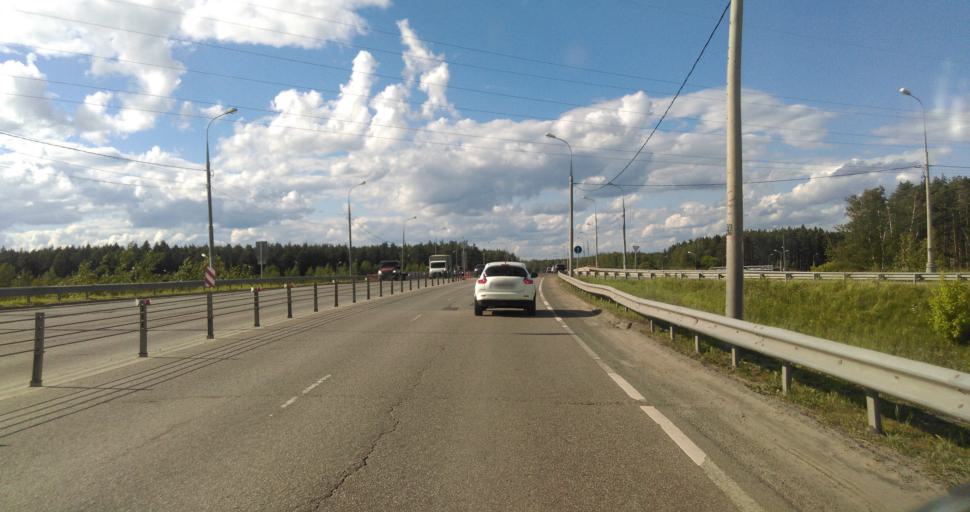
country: RU
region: Moskovskaya
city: Vostryakovo
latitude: 55.4032
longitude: 37.7857
